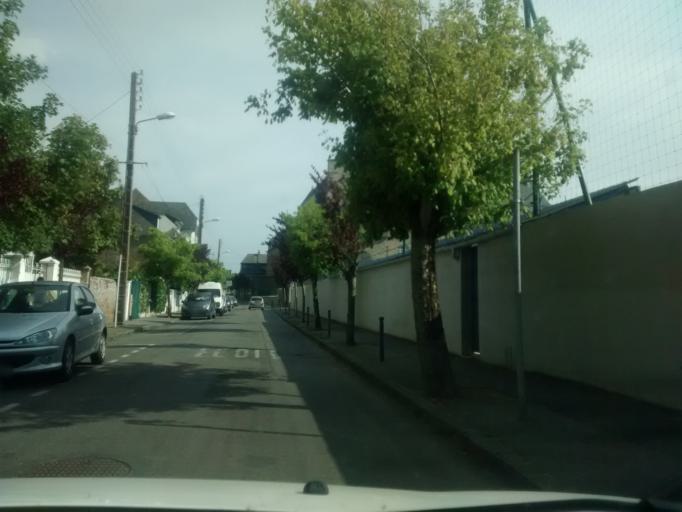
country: FR
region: Brittany
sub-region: Departement d'Ille-et-Vilaine
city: Saint-Malo
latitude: 48.6602
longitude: -1.9828
